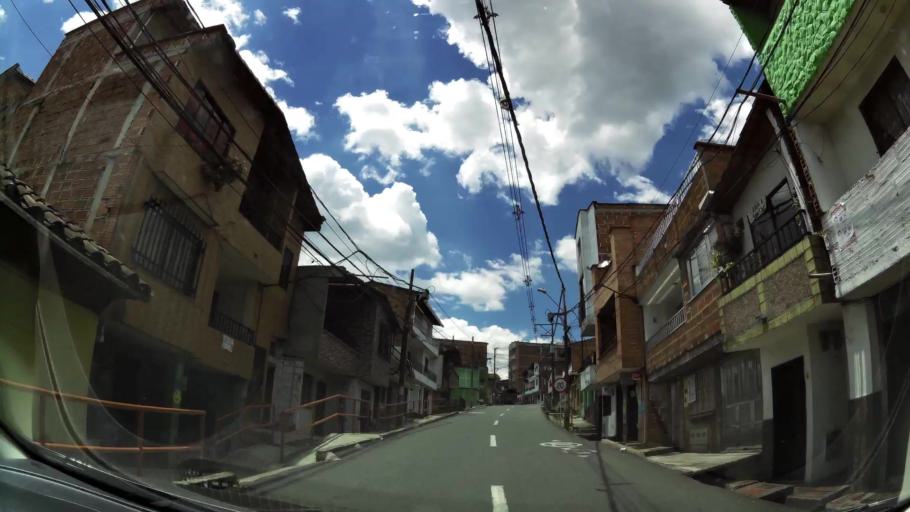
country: CO
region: Antioquia
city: La Estrella
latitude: 6.1560
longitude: -75.6392
